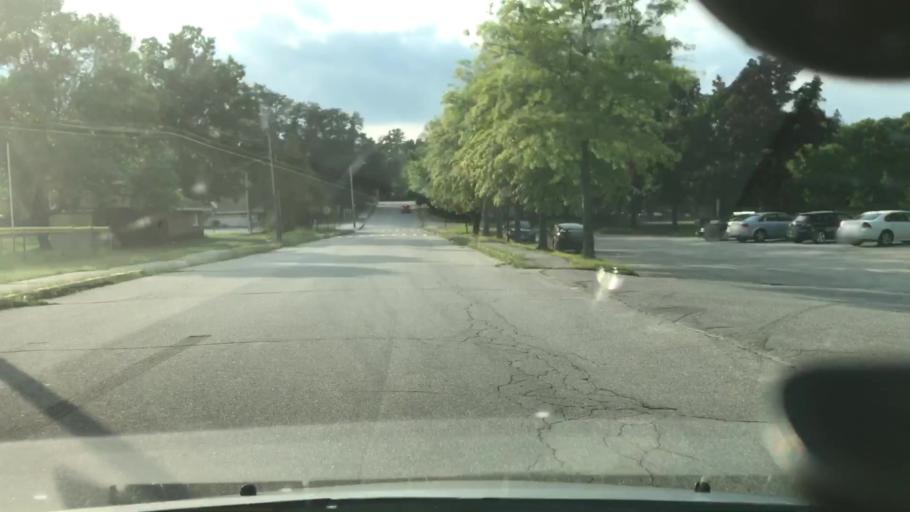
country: US
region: New Hampshire
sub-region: Hillsborough County
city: Manchester
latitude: 42.9719
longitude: -71.4775
